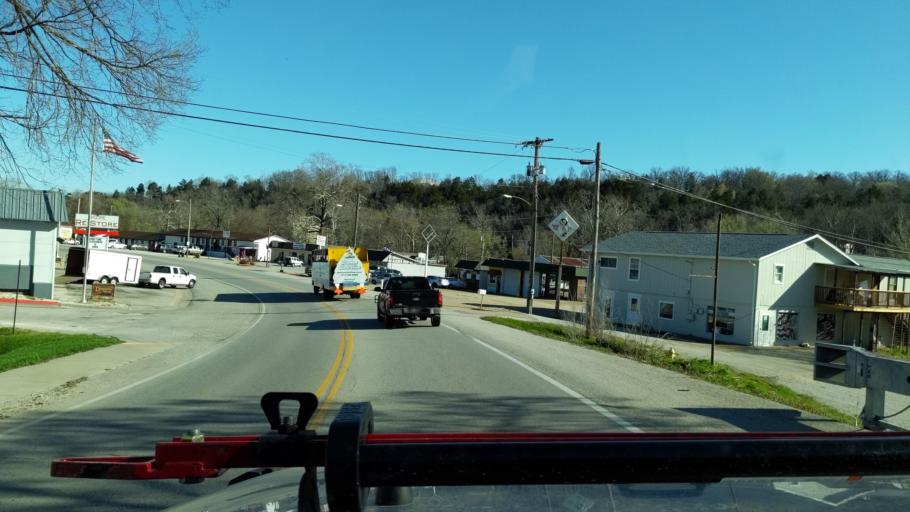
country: US
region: Missouri
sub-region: Taney County
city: Hollister
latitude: 36.6224
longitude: -93.2148
